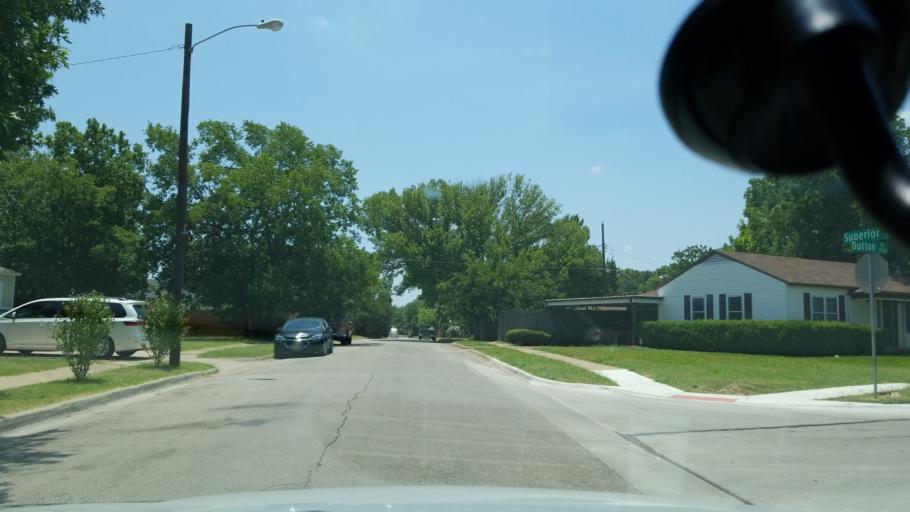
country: US
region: Texas
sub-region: Dallas County
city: Cockrell Hill
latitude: 32.7259
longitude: -96.8639
